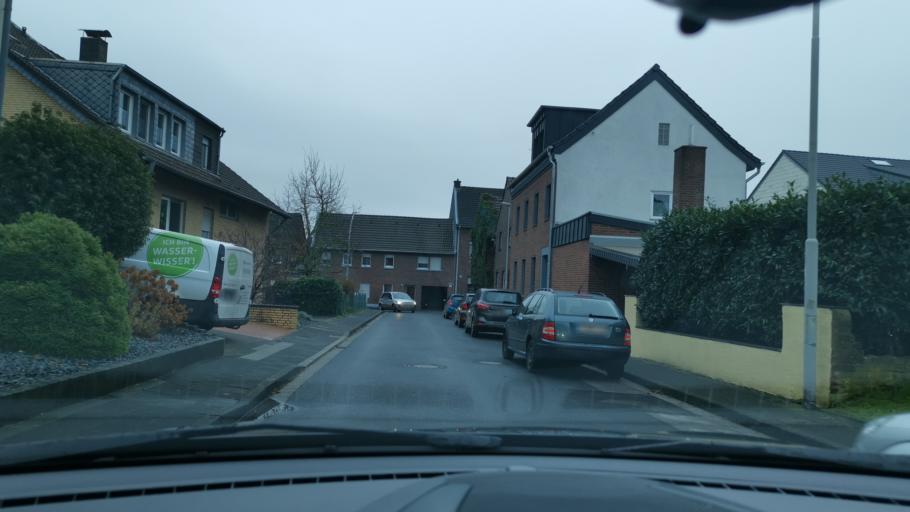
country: DE
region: North Rhine-Westphalia
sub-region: Regierungsbezirk Dusseldorf
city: Juchen
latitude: 51.1042
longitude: 6.5032
